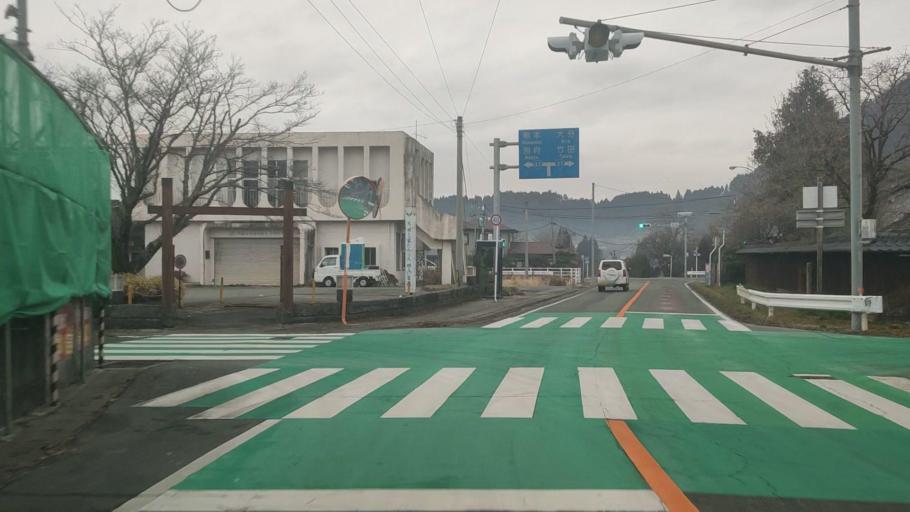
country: JP
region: Kumamoto
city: Aso
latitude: 32.9369
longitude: 131.1378
